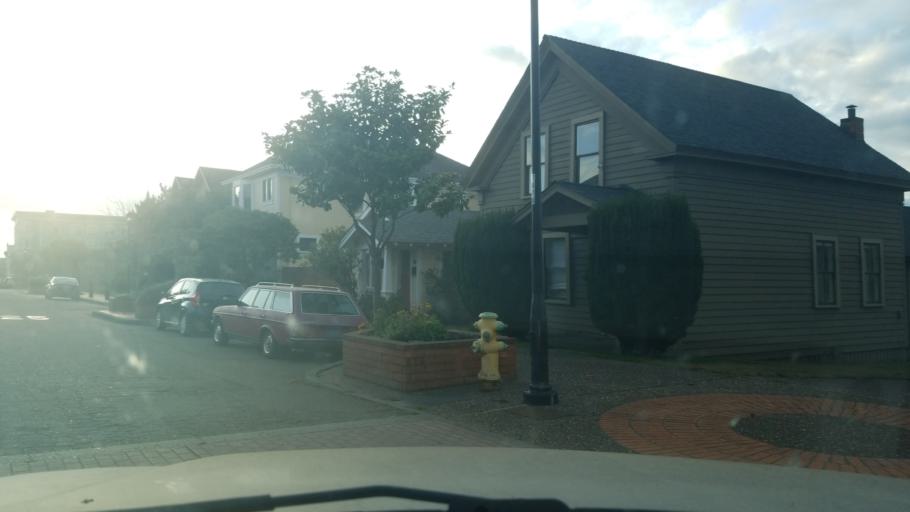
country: US
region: California
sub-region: Humboldt County
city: Eureka
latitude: 40.8049
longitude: -124.1633
